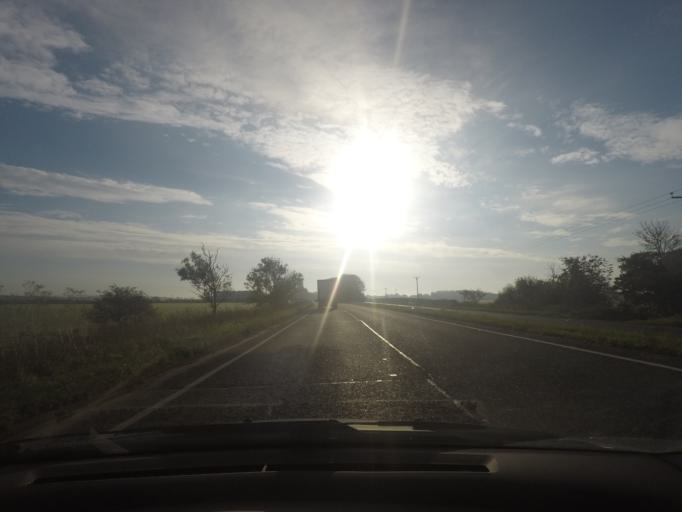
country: GB
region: England
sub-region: East Riding of Yorkshire
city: Hayton
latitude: 53.8951
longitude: -0.7427
